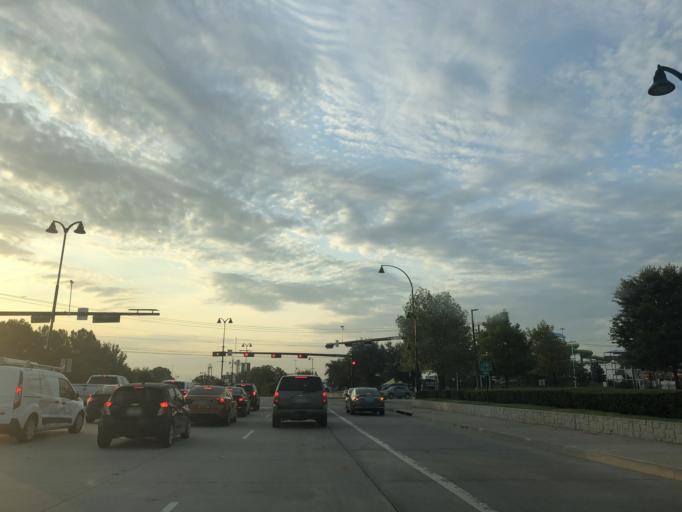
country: US
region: Texas
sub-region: Tarrant County
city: Arlington
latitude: 32.7638
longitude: -97.0859
